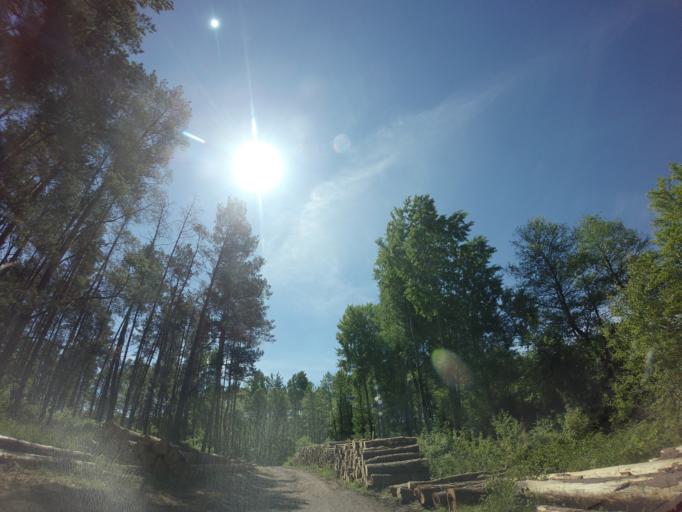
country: PL
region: West Pomeranian Voivodeship
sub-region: Powiat choszczenski
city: Drawno
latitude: 53.2985
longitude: 15.6915
